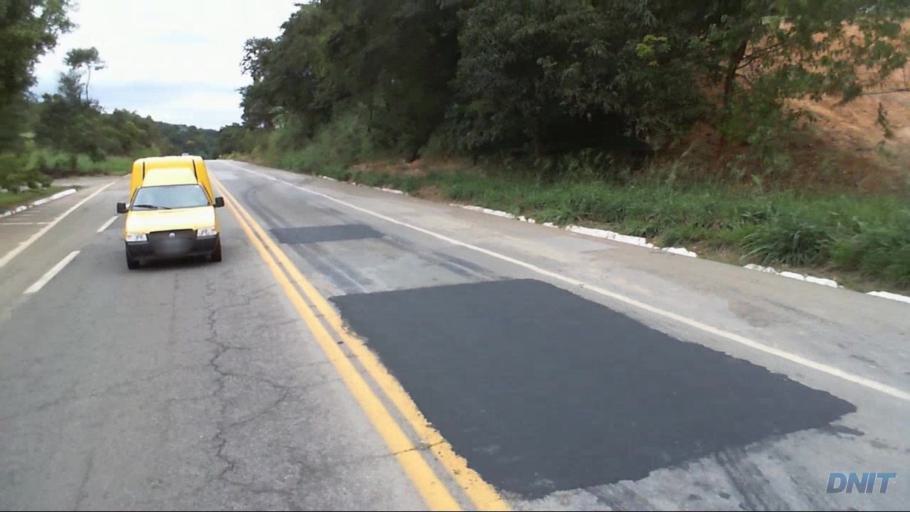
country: BR
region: Minas Gerais
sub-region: Barao De Cocais
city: Barao de Cocais
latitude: -19.7977
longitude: -43.4233
